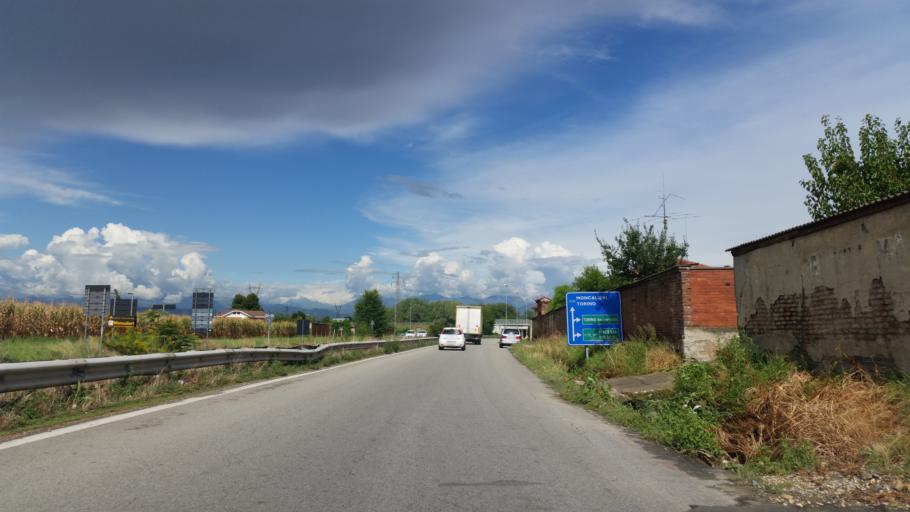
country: IT
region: Piedmont
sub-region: Provincia di Torino
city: Santena
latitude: 44.9572
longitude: 7.7869
